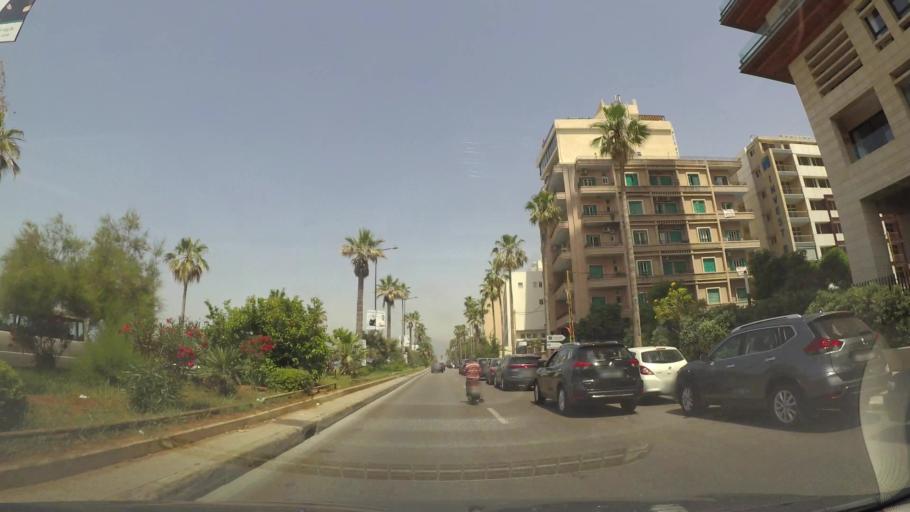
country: LB
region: Beyrouth
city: Ra's Bayrut
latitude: 33.9019
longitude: 35.4769
